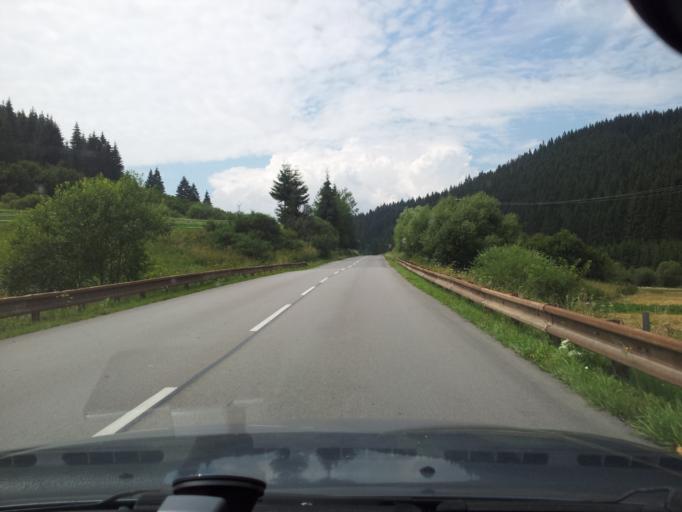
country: SK
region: Zilinsky
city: Oravska Lesna
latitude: 49.3795
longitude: 19.3315
